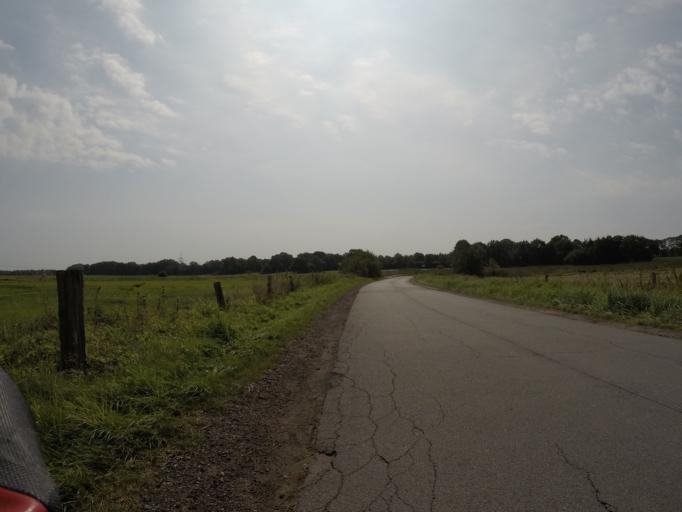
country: DE
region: Schleswig-Holstein
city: Henstedt-Ulzburg
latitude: 53.7703
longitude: 10.0192
